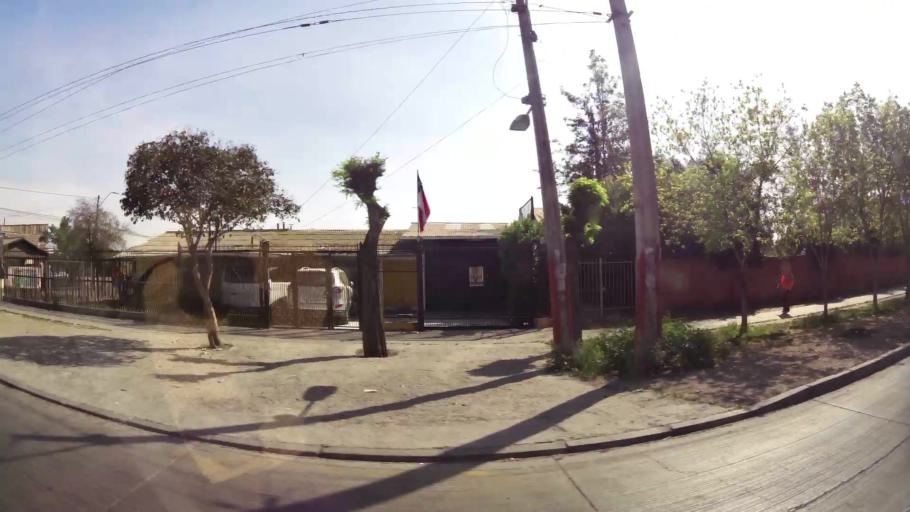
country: CL
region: Santiago Metropolitan
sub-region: Provincia de Santiago
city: Lo Prado
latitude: -33.4298
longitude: -70.7393
